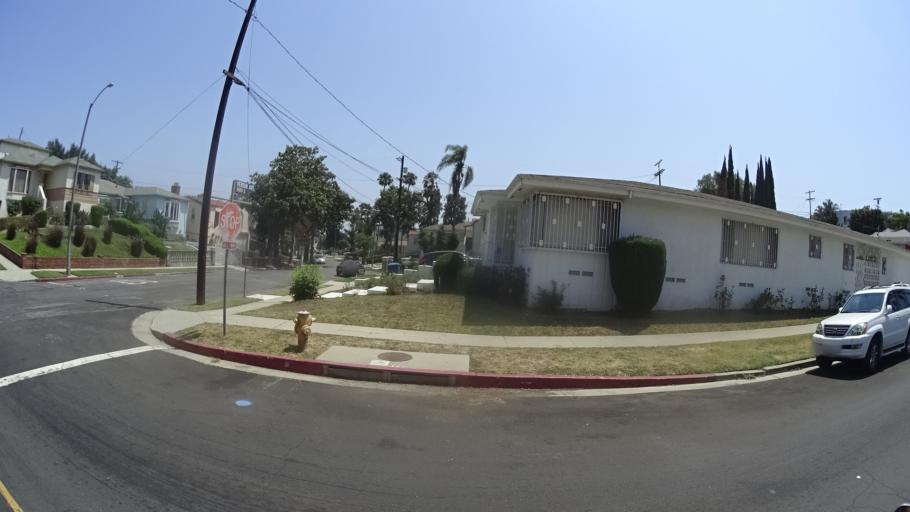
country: US
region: California
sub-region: Los Angeles County
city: View Park-Windsor Hills
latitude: 33.9853
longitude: -118.3464
